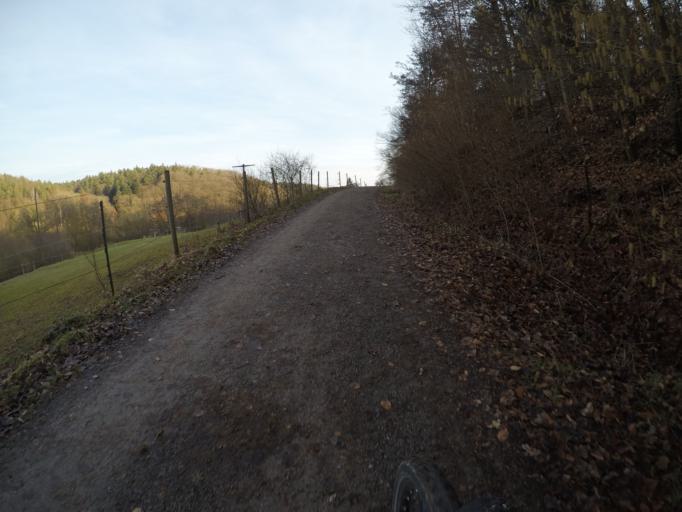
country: DE
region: Baden-Wuerttemberg
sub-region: Regierungsbezirk Stuttgart
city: Steinenbronn
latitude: 48.6494
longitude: 9.1011
